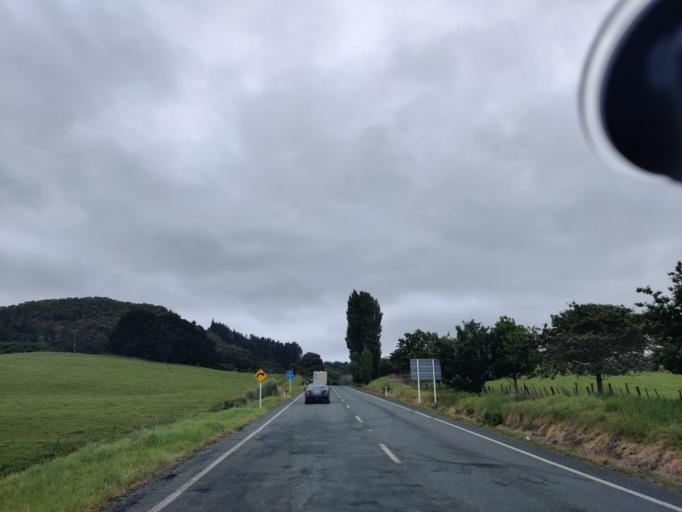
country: NZ
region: Northland
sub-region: Whangarei
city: Ruakaka
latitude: -36.0977
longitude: 174.4253
